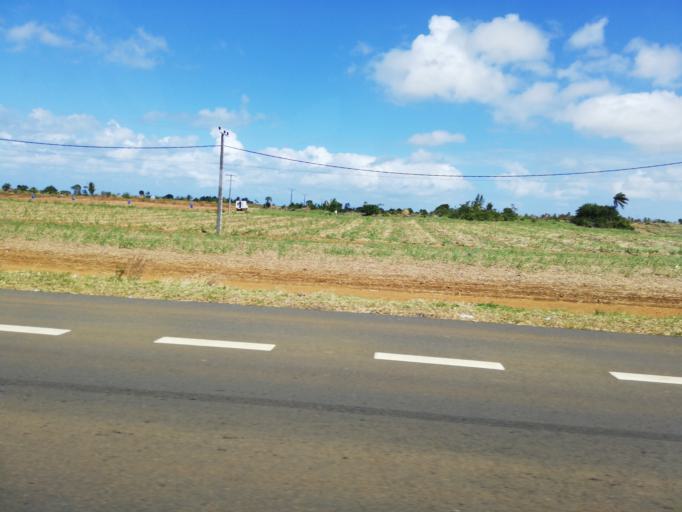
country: MU
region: Grand Port
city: Plaine Magnien
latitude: -20.4408
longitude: 57.6660
